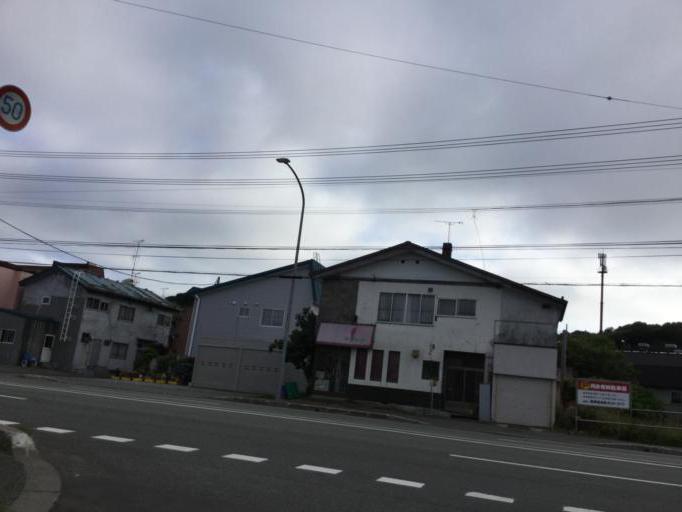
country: JP
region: Hokkaido
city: Wakkanai
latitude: 45.4027
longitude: 141.6783
